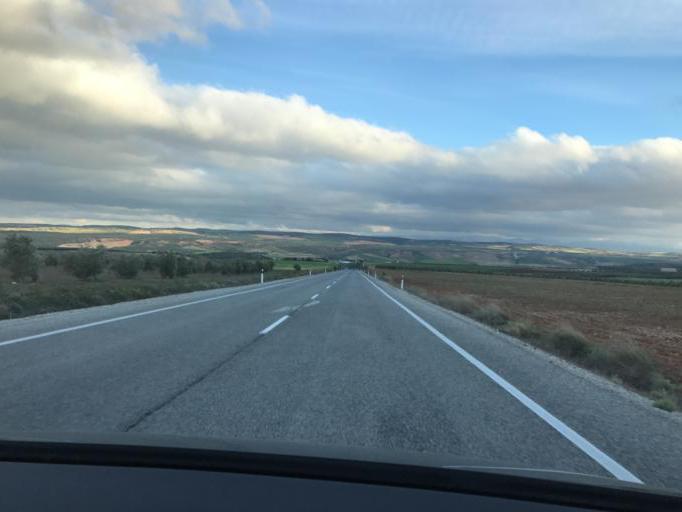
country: ES
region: Andalusia
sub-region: Provincia de Jaen
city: Guadahortuna
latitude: 37.5801
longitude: -3.4044
